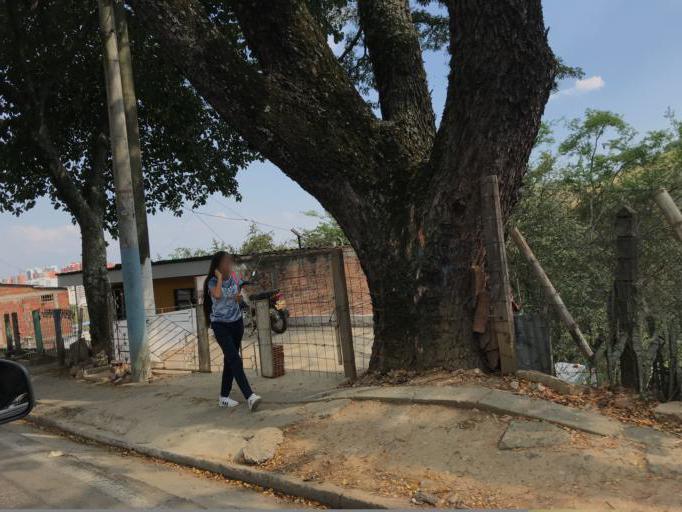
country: CO
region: Valle del Cauca
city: Cali
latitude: 3.4504
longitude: -76.5628
